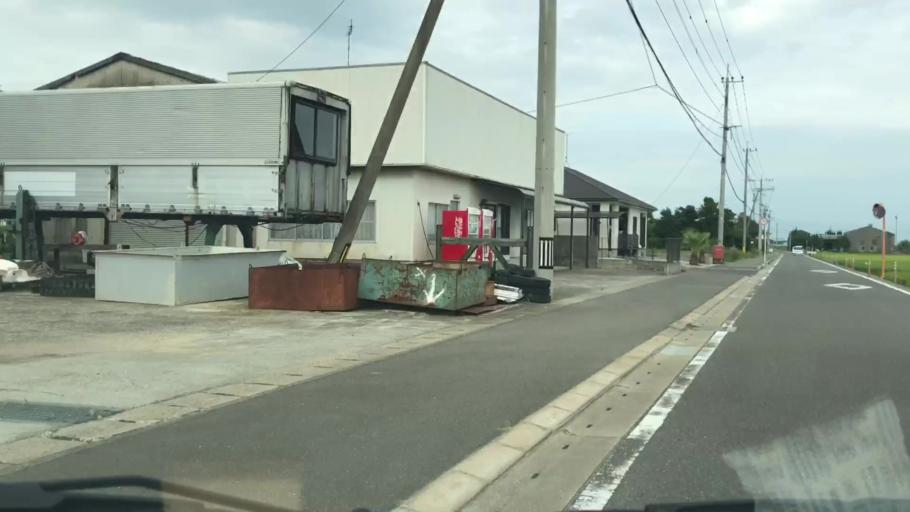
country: JP
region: Saga Prefecture
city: Saga-shi
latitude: 33.2892
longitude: 130.2246
